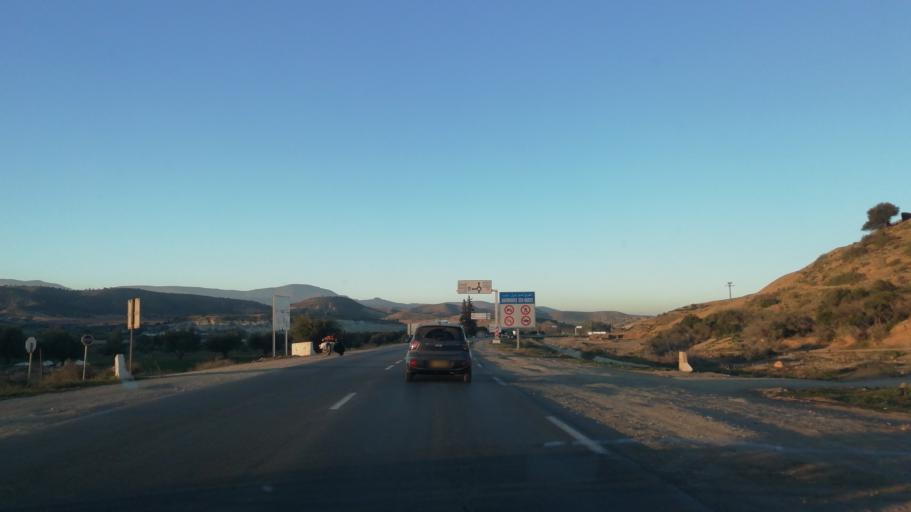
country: DZ
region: Tlemcen
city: Nedroma
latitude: 34.9048
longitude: -1.6406
